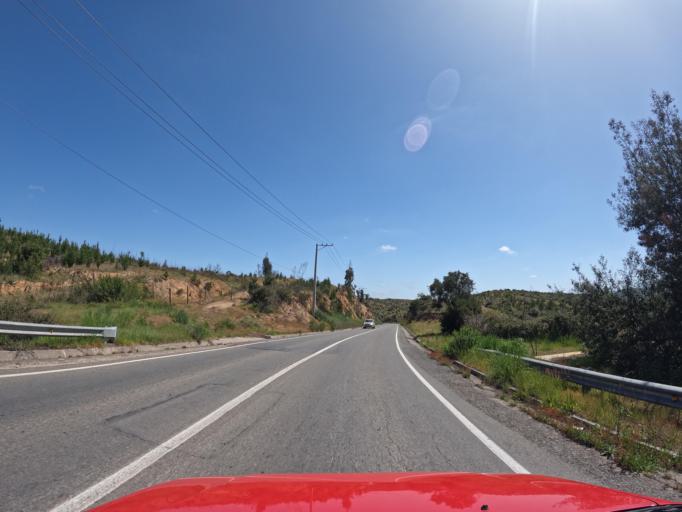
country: CL
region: O'Higgins
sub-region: Provincia de Colchagua
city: Santa Cruz
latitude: -34.6620
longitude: -71.8474
